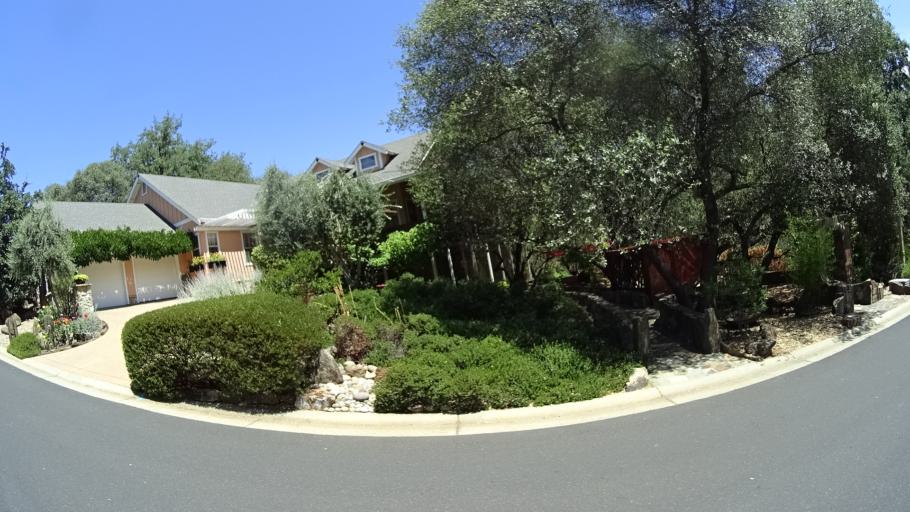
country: US
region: California
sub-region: Calaveras County
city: Angels Camp
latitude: 38.0684
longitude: -120.5633
